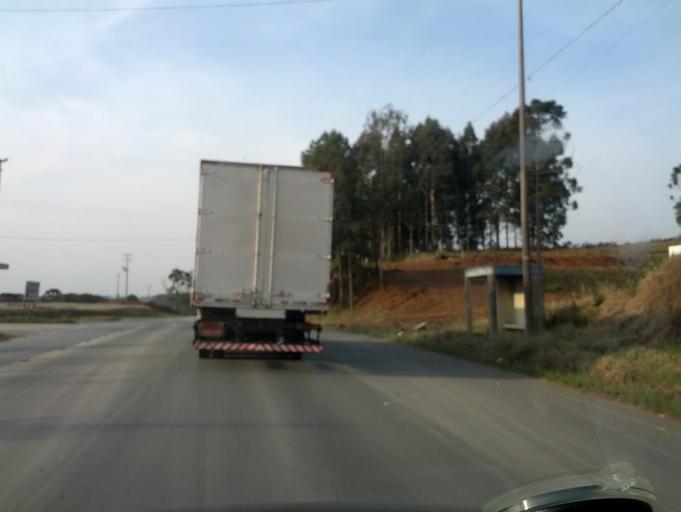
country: BR
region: Santa Catarina
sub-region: Otacilio Costa
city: Otacilio Costa
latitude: -27.5241
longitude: -50.1368
